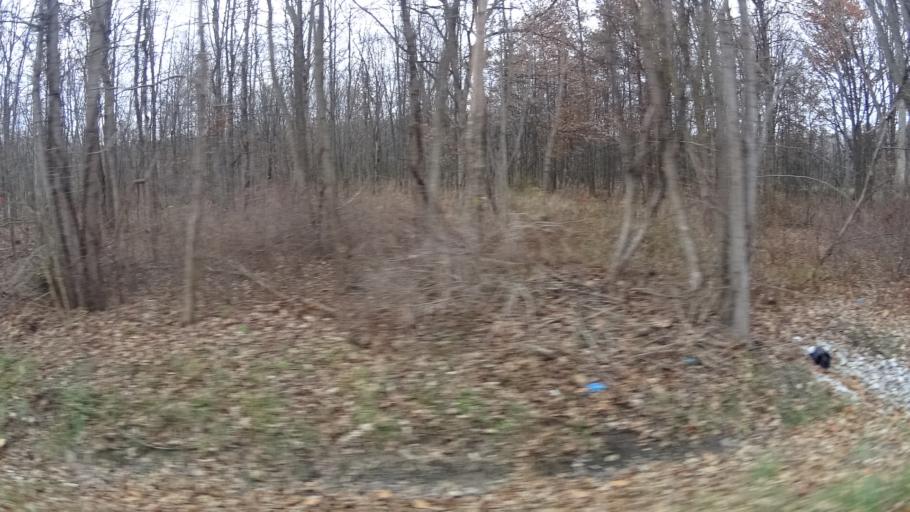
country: US
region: Ohio
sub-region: Cuyahoga County
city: Olmsted Falls
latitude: 41.3251
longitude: -81.8962
